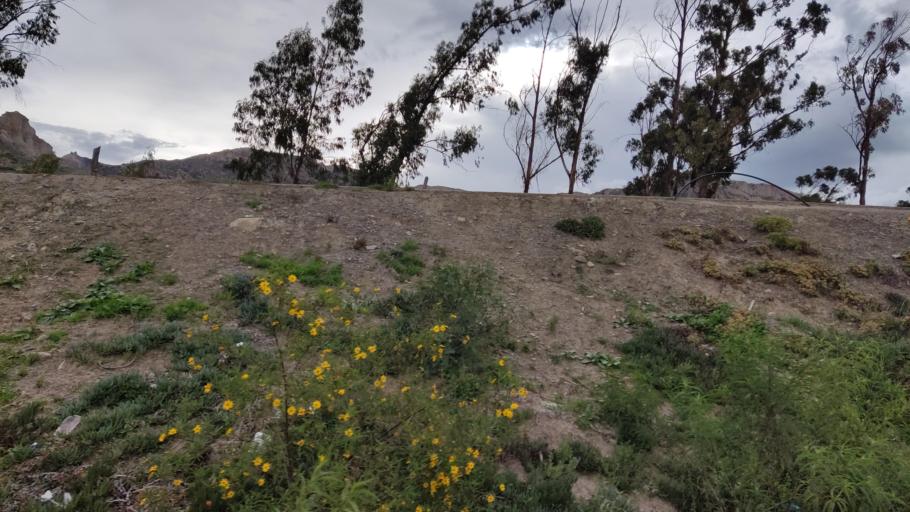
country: BO
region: La Paz
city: La Paz
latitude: -16.5842
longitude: -68.0782
